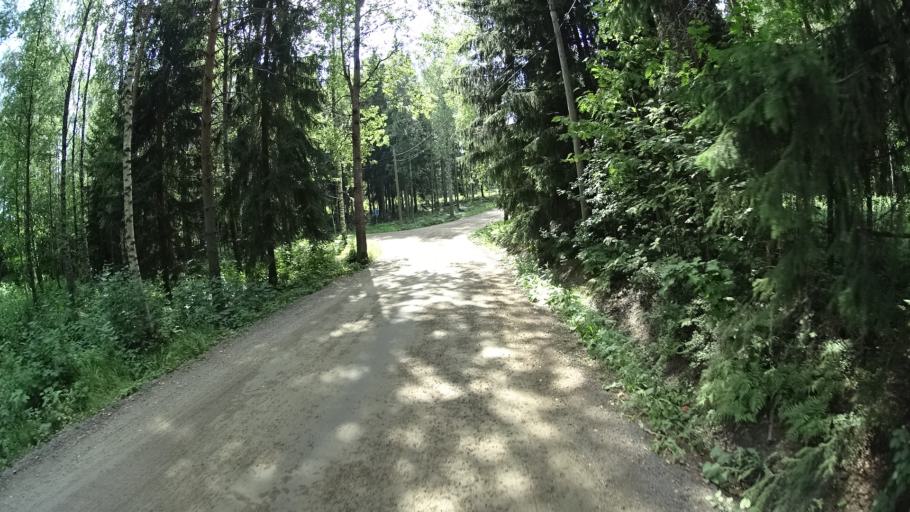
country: FI
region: Uusimaa
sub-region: Porvoo
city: Porvoo
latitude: 60.3929
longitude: 25.7073
